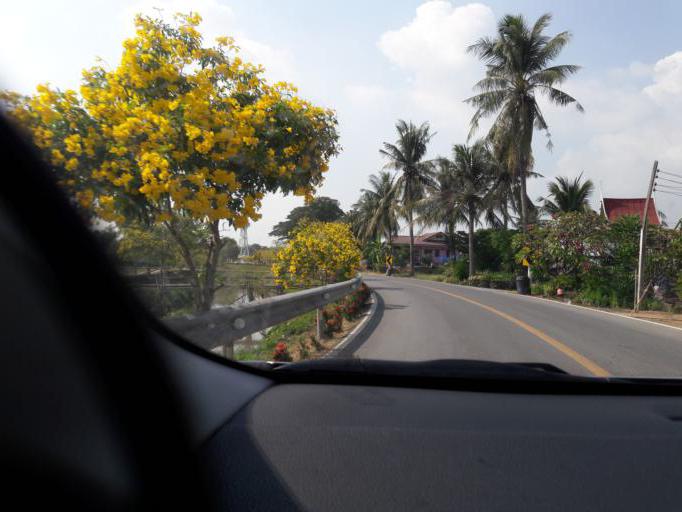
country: TH
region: Ang Thong
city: Pa Mok
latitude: 14.5328
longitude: 100.3904
